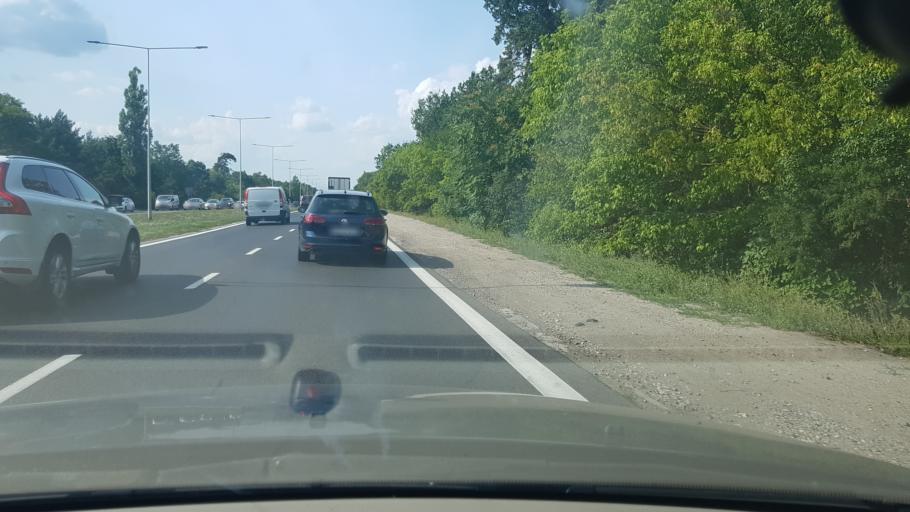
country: PL
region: Masovian Voivodeship
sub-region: Warszawa
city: Bielany
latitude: 52.3098
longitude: 20.9264
